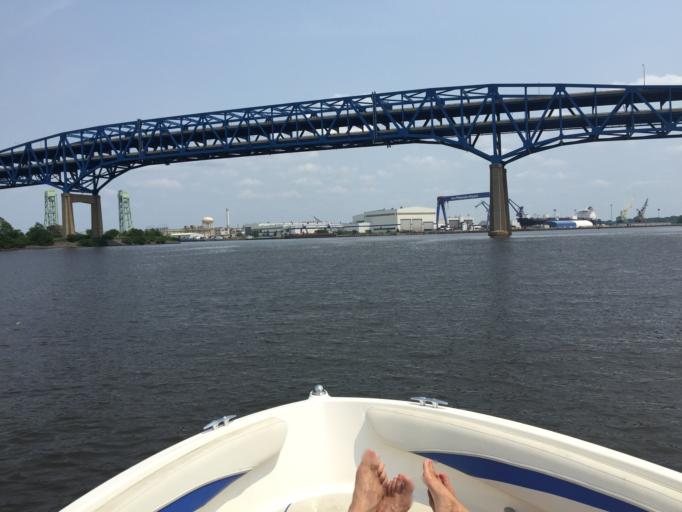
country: US
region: New Jersey
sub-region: Gloucester County
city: National Park
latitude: 39.8936
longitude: -75.2001
